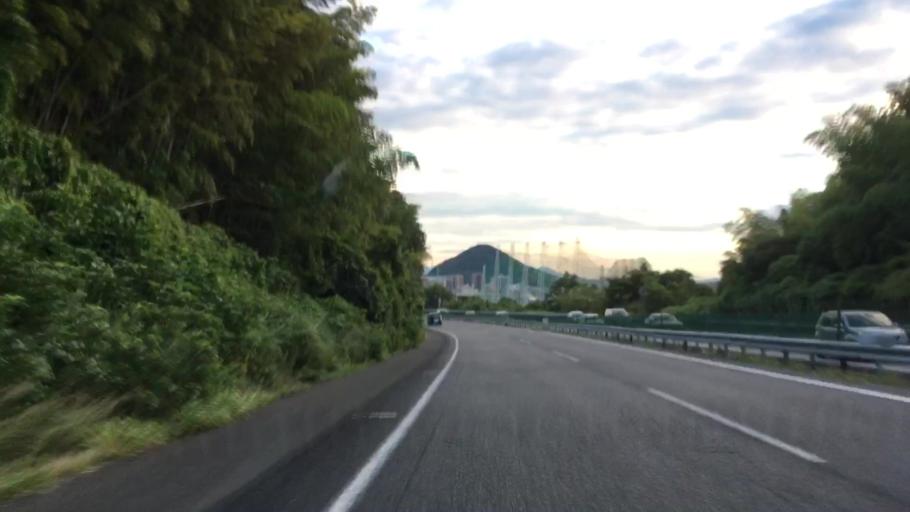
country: JP
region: Yamaguchi
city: Shimonoseki
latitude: 34.0209
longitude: 130.9590
